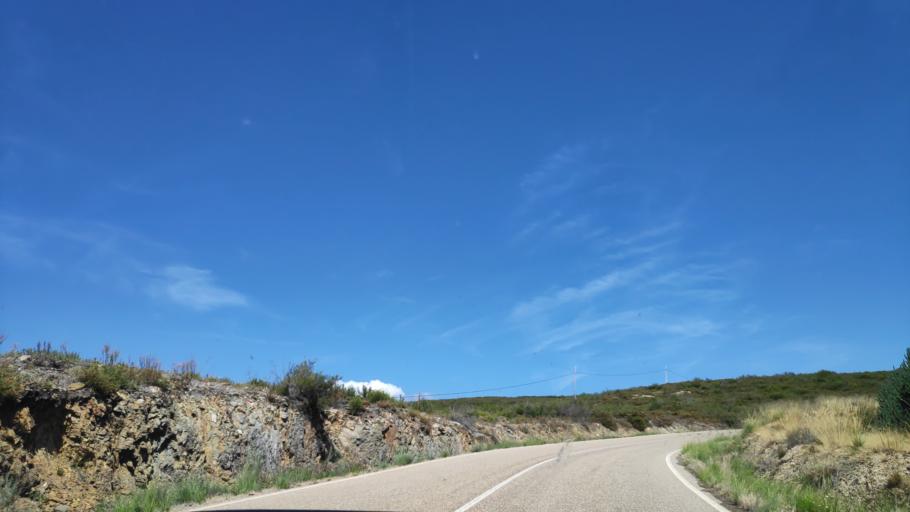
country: ES
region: Castille and Leon
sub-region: Provincia de Zamora
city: Requejo
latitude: 42.0079
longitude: -6.6954
